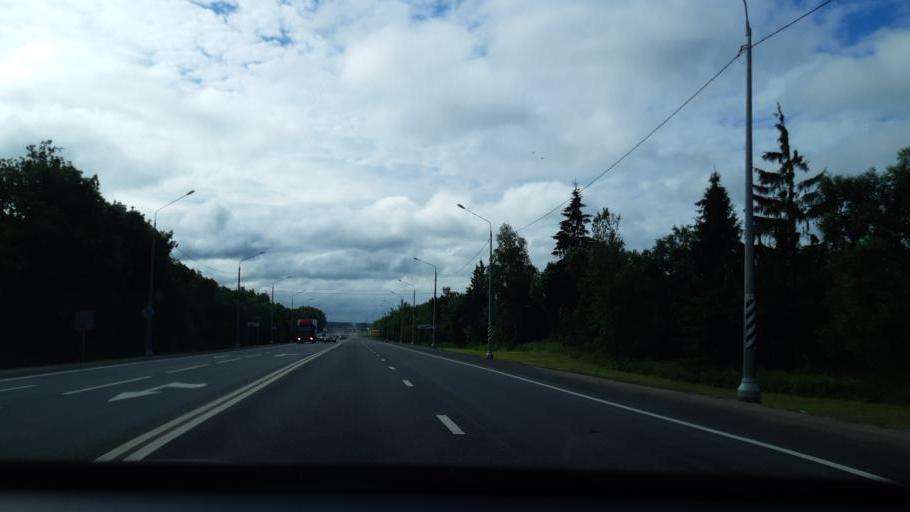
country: RU
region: Smolensk
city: Smolensk
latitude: 54.7155
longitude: 32.1086
